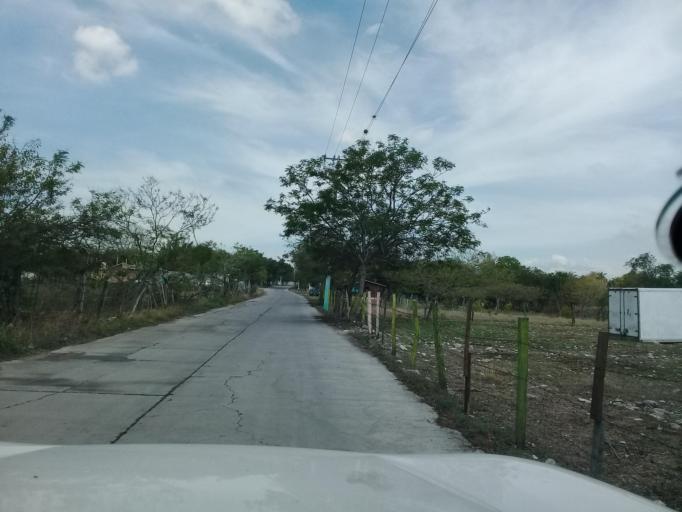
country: MX
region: Veracruz
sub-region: Emiliano Zapata
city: Plan del Rio
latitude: 19.3528
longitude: -96.6418
